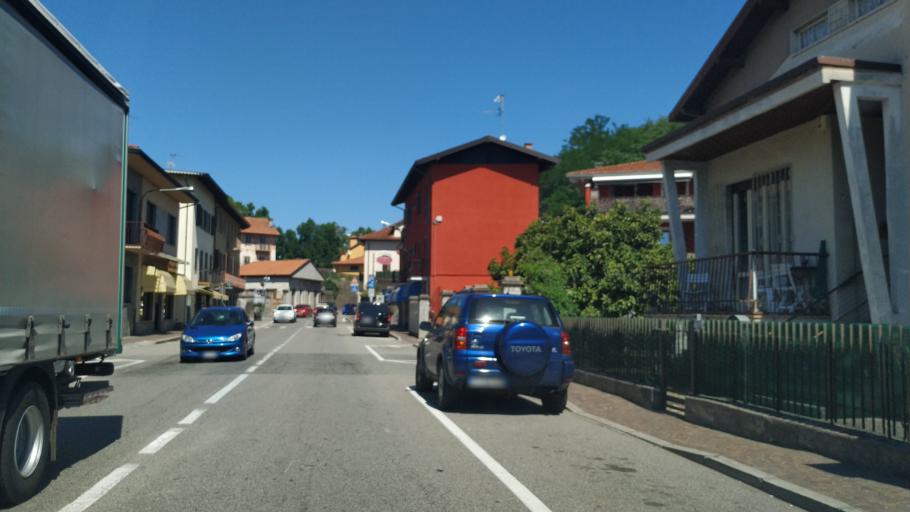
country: IT
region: Piedmont
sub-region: Provincia di Novara
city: Oleggio Castello
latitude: 45.7486
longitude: 8.5279
